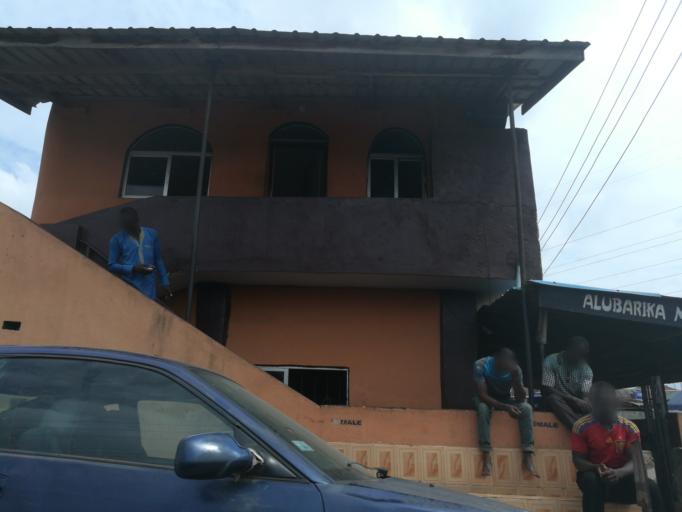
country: NG
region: Lagos
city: Somolu
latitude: 6.5440
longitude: 3.3931
